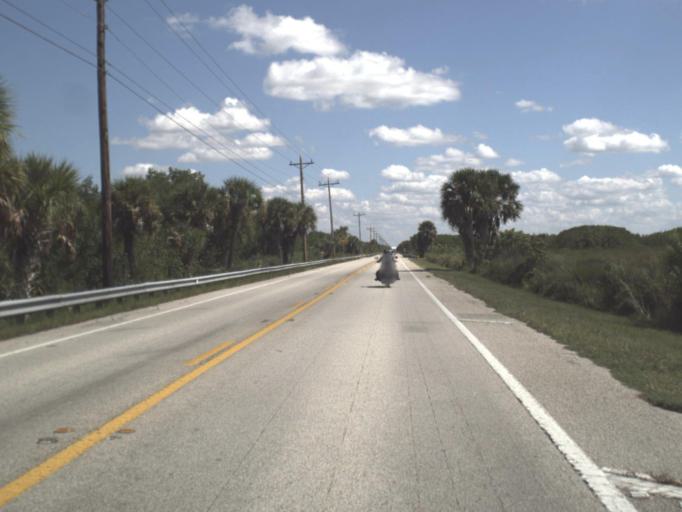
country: US
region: Florida
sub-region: Collier County
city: Marco
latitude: 25.9371
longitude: -81.4586
